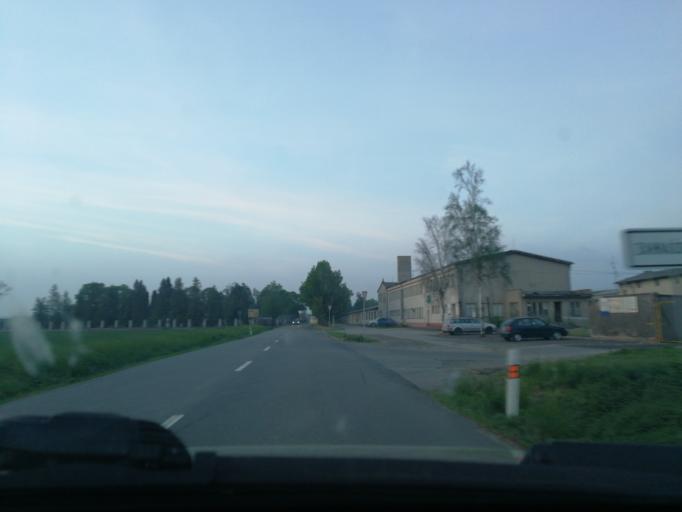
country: CZ
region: Zlin
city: Holesov
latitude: 49.3010
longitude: 17.5580
